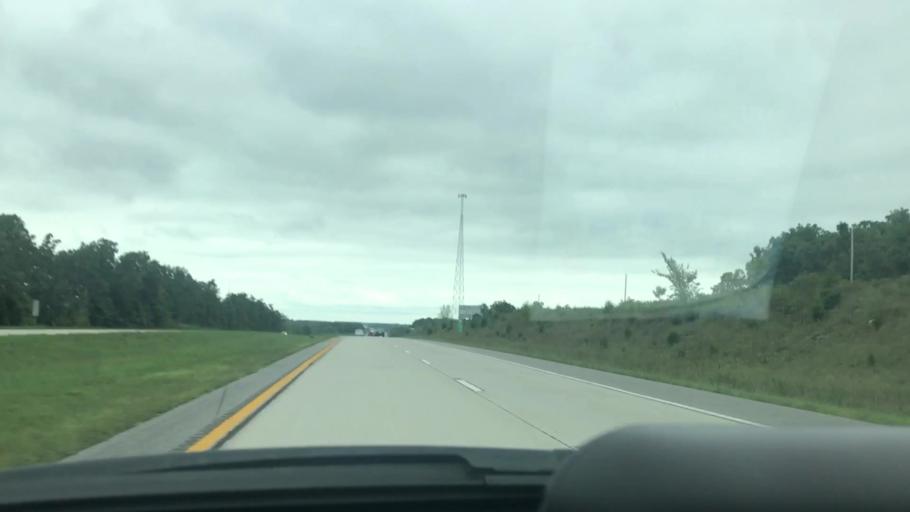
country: US
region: Missouri
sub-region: Greene County
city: Fair Grove
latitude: 37.5055
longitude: -93.1388
